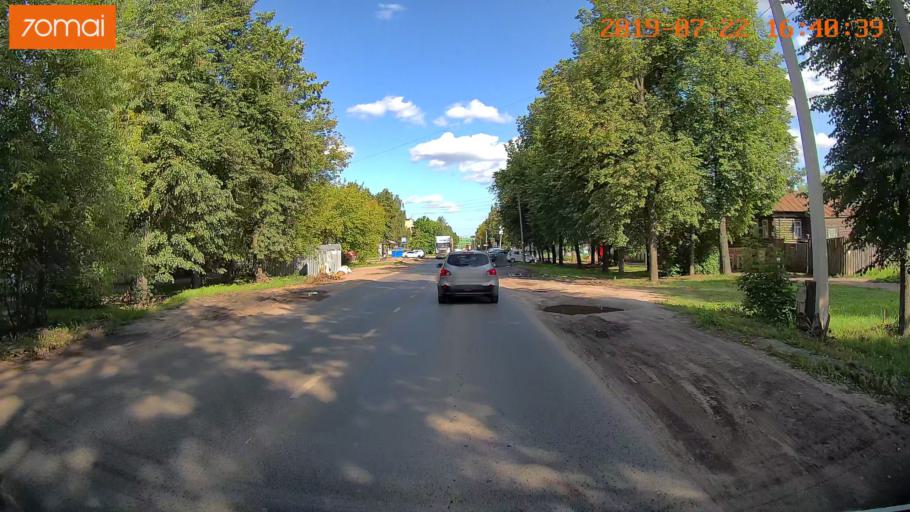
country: RU
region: Ivanovo
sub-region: Gorod Ivanovo
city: Ivanovo
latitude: 57.0233
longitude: 40.9590
